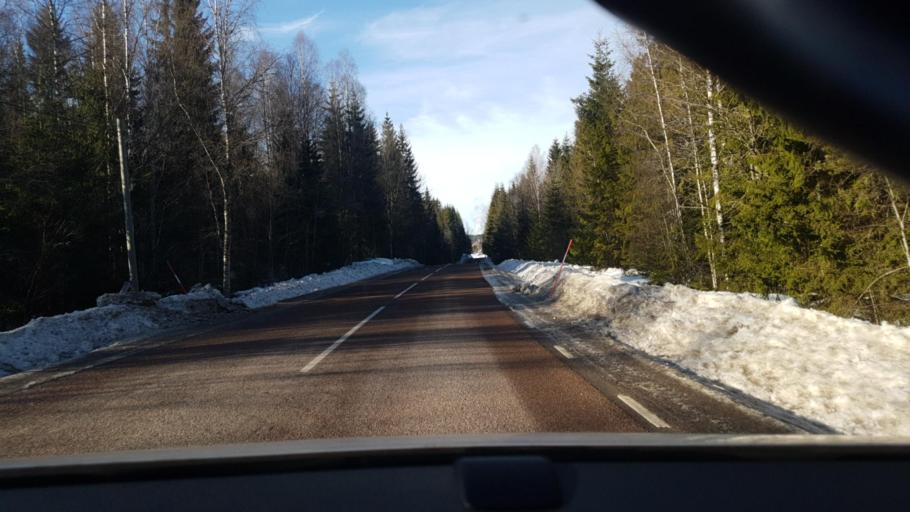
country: SE
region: Vaermland
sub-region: Eda Kommun
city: Charlottenberg
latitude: 59.8107
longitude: 12.1620
